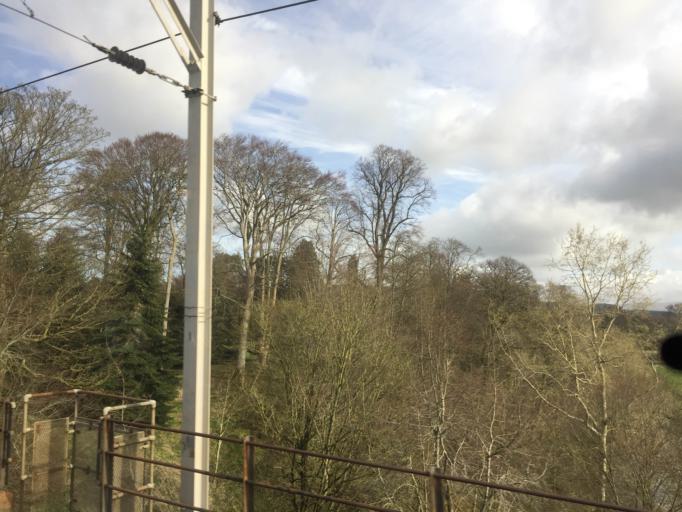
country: GB
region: England
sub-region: Cumbria
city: Penrith
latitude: 54.6476
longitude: -2.7640
